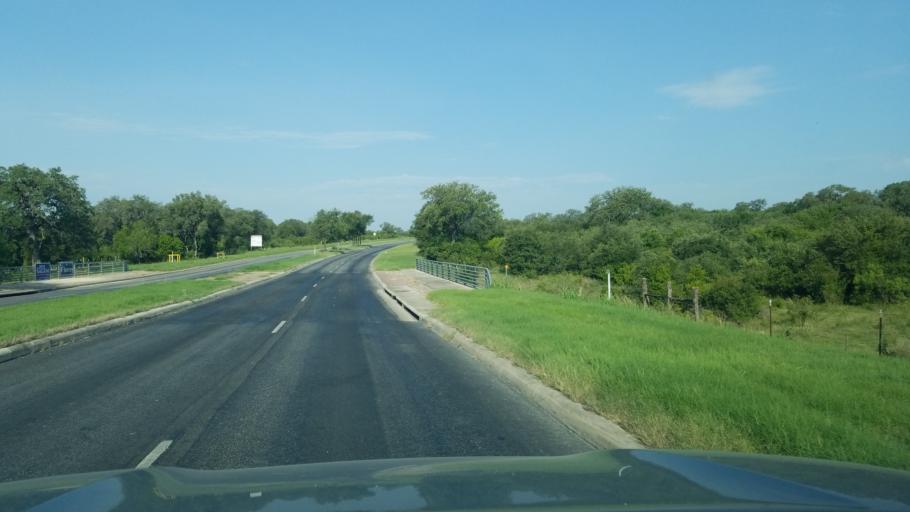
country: US
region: Texas
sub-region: Bexar County
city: Leon Valley
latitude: 29.4602
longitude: -98.7379
